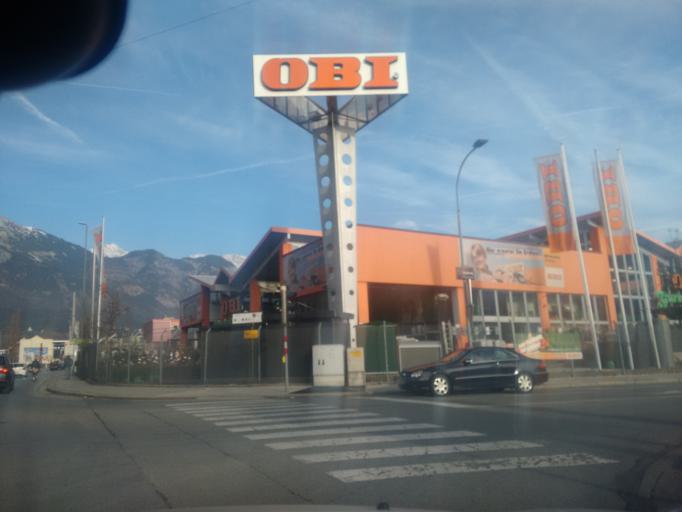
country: AT
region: Tyrol
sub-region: Politischer Bezirk Innsbruck Land
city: Ampass
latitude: 47.2671
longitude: 11.4253
